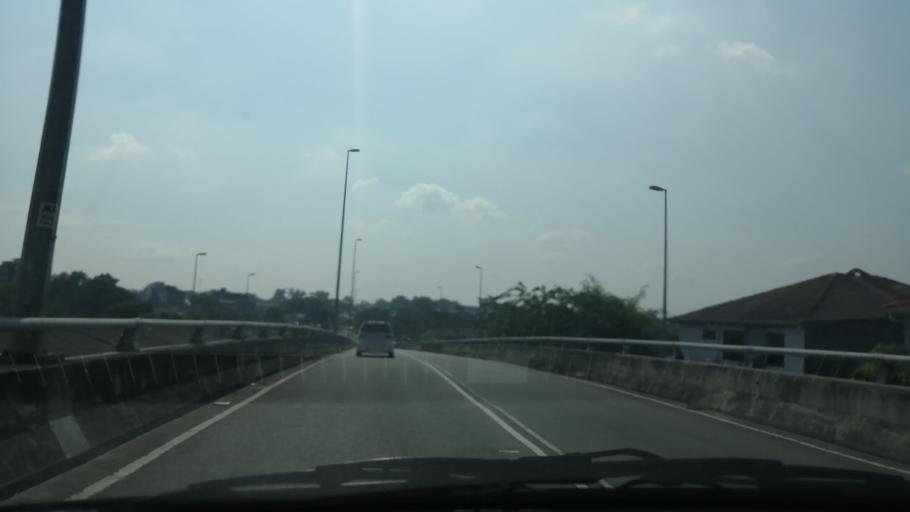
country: MY
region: Kedah
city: Sungai Petani
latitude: 5.6362
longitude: 100.4896
